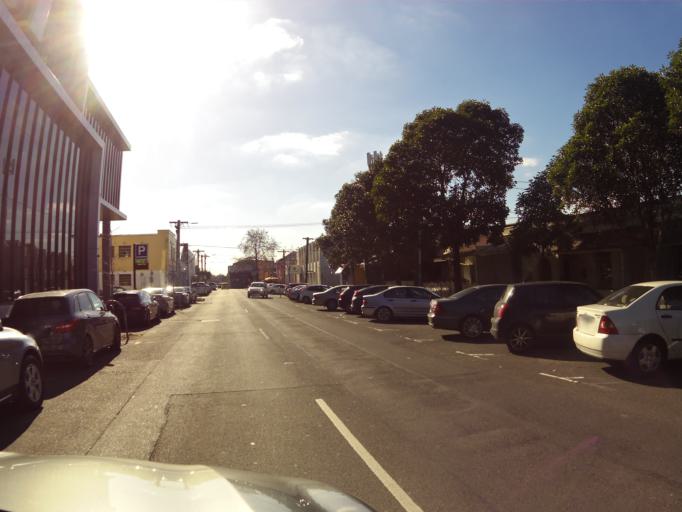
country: AU
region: Victoria
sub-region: Melbourne
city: East Melbourne
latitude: -37.8111
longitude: 144.9936
